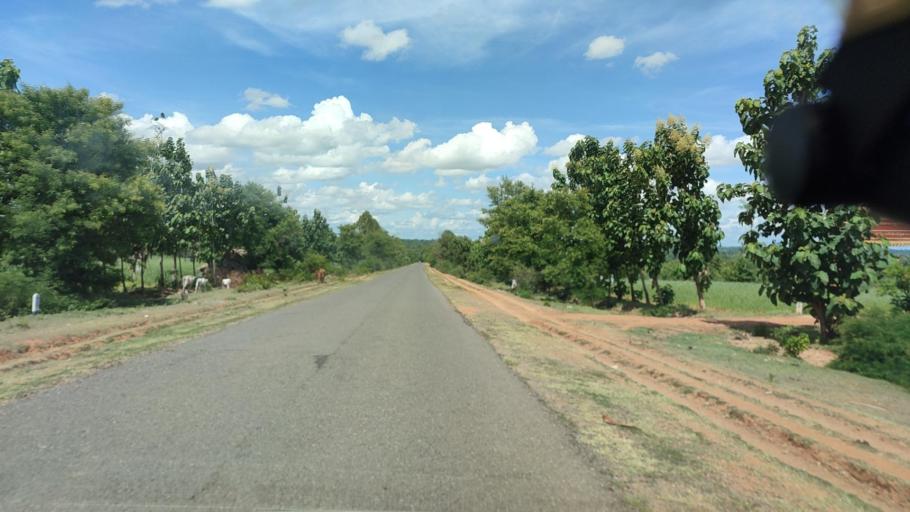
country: MM
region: Magway
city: Magway
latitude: 20.1904
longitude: 95.1779
